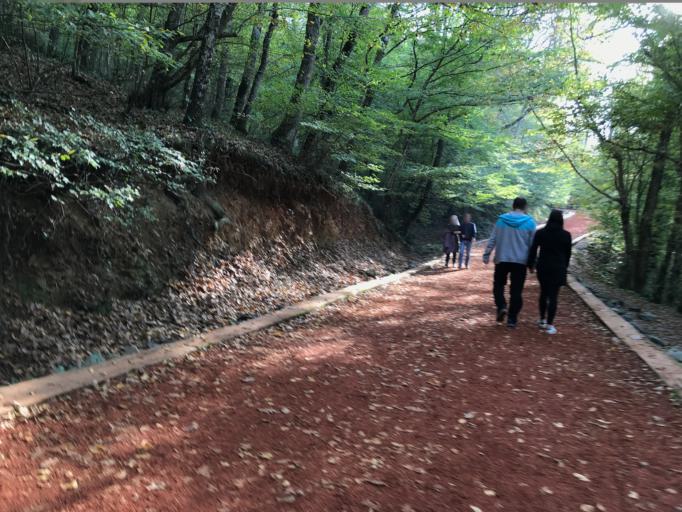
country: TR
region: Istanbul
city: Kemerburgaz
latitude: 41.1824
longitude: 28.9625
